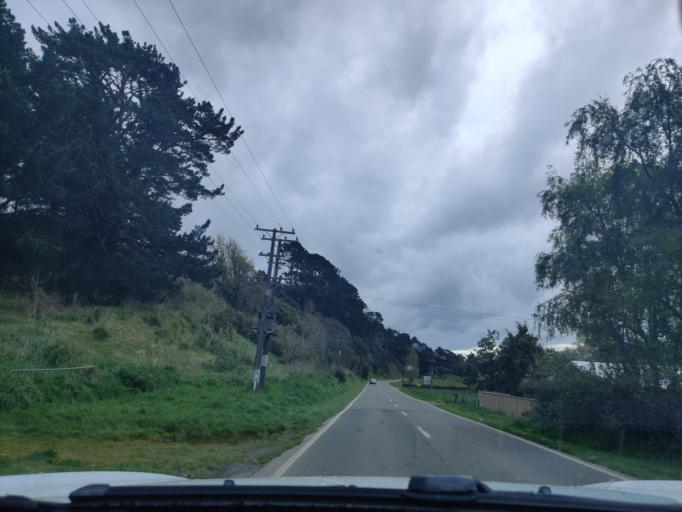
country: NZ
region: Manawatu-Wanganui
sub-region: Palmerston North City
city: Palmerston North
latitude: -40.3255
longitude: 175.7448
